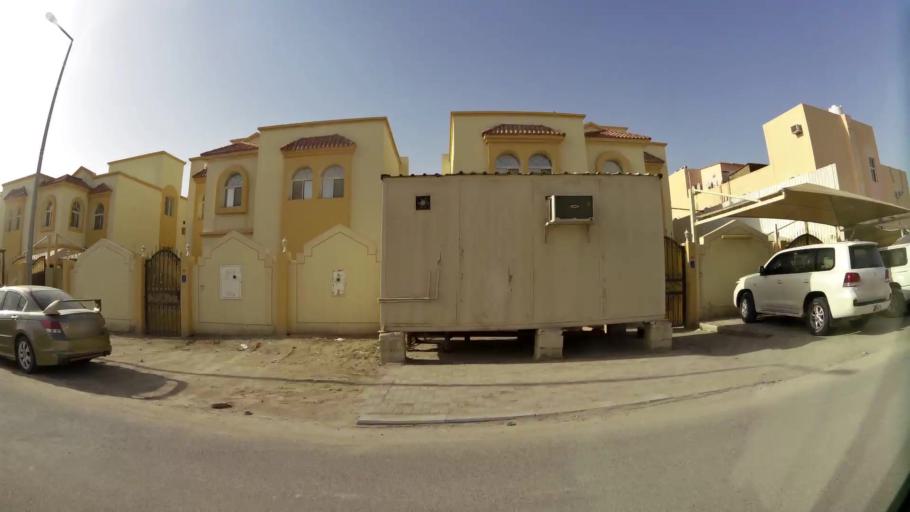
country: QA
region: Baladiyat ar Rayyan
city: Ar Rayyan
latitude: 25.3416
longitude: 51.4428
